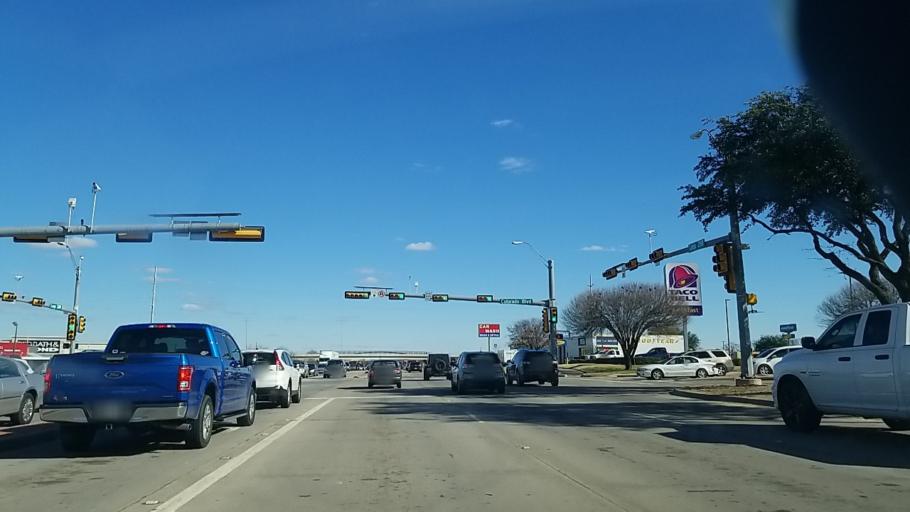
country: US
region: Texas
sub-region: Denton County
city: Denton
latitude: 33.1889
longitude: -97.1045
